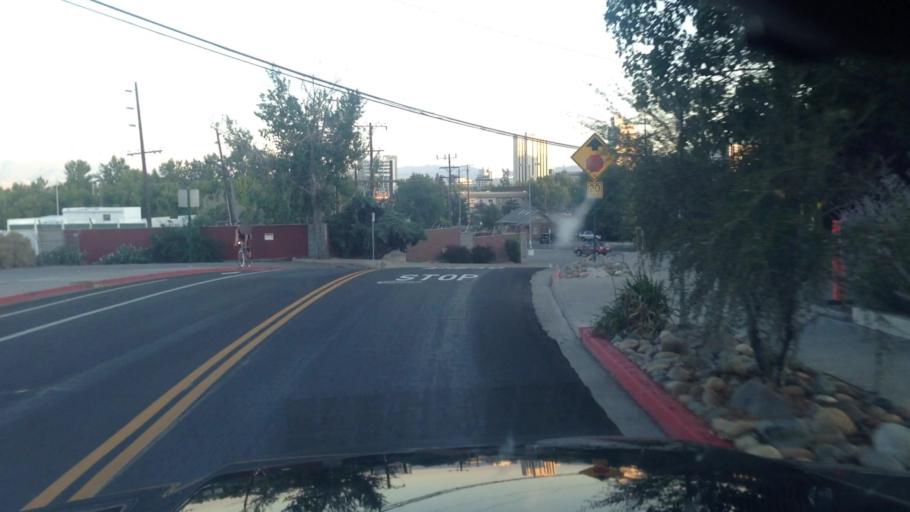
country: US
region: Nevada
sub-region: Washoe County
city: Reno
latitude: 39.5386
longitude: -119.8110
